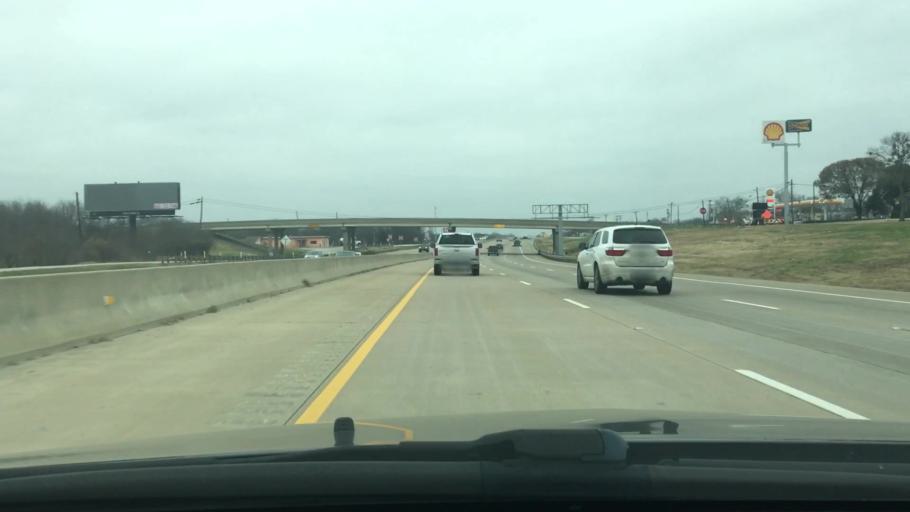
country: US
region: Texas
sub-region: Ellis County
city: Ennis
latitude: 32.2459
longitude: -96.4971
